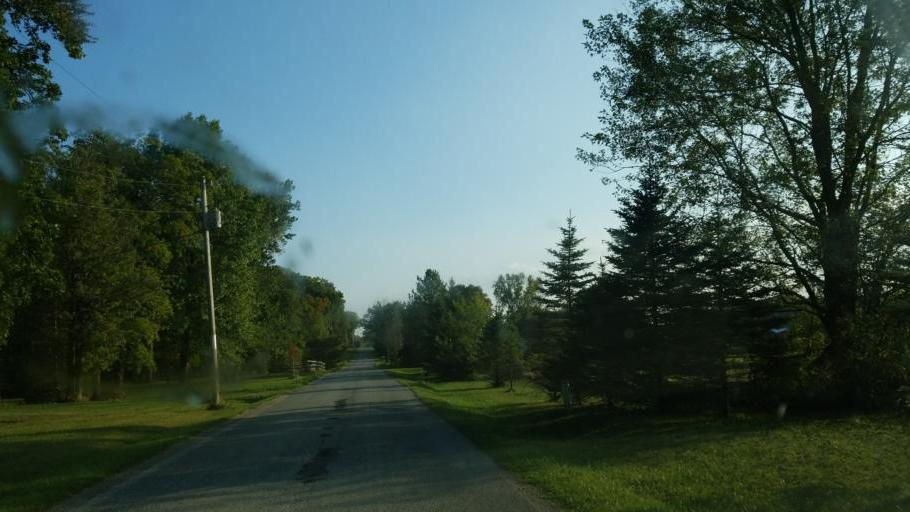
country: US
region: Ohio
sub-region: Knox County
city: Centerburg
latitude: 40.4273
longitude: -82.6599
